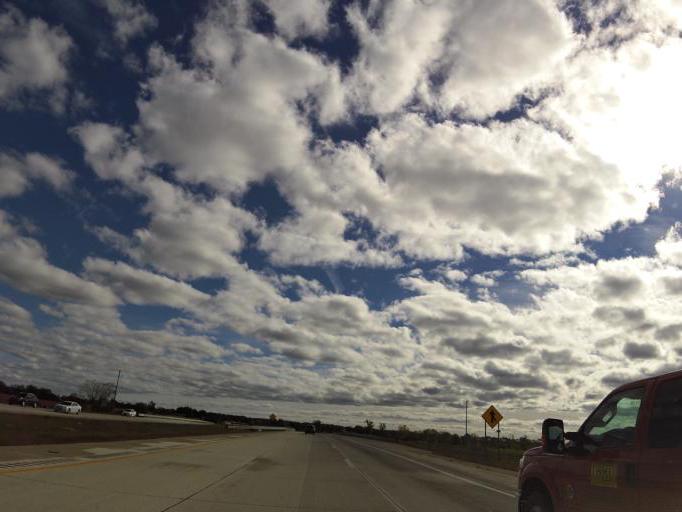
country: US
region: Michigan
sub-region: Genesee County
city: Davison
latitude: 43.0164
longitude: -83.5580
